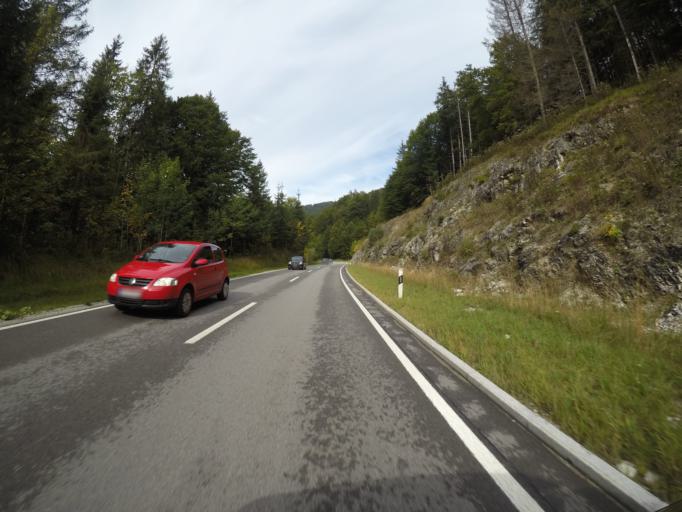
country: DE
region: Bavaria
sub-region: Upper Bavaria
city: Lenggries
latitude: 47.5823
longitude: 11.6090
